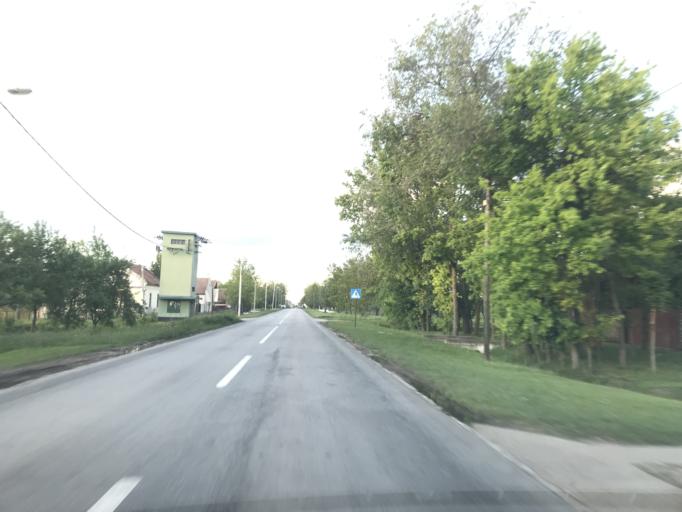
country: RS
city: Cestereg
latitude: 45.5604
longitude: 20.5279
